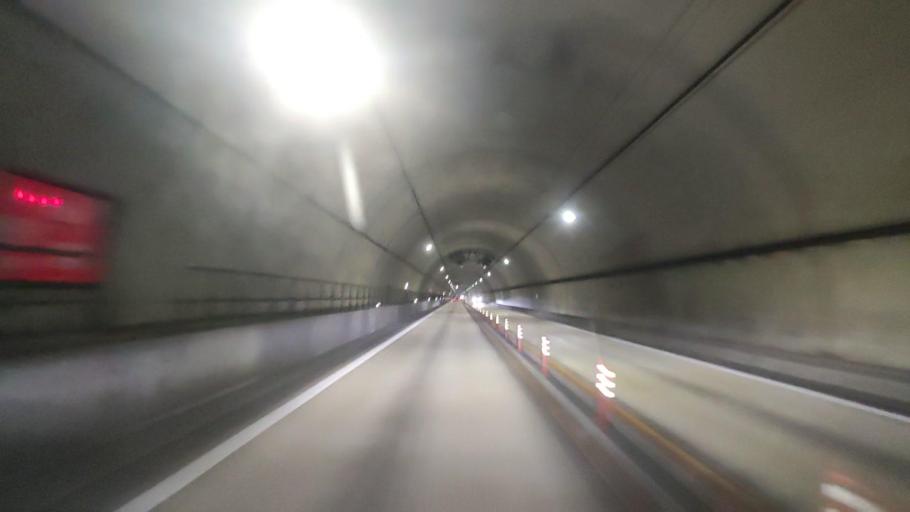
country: JP
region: Wakayama
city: Tanabe
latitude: 33.5679
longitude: 135.4896
